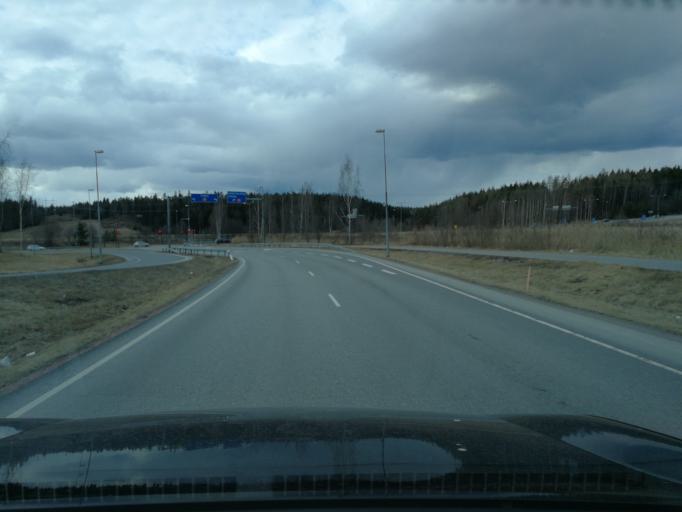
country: FI
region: Varsinais-Suomi
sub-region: Turku
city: Kaarina
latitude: 60.4718
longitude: 22.3654
